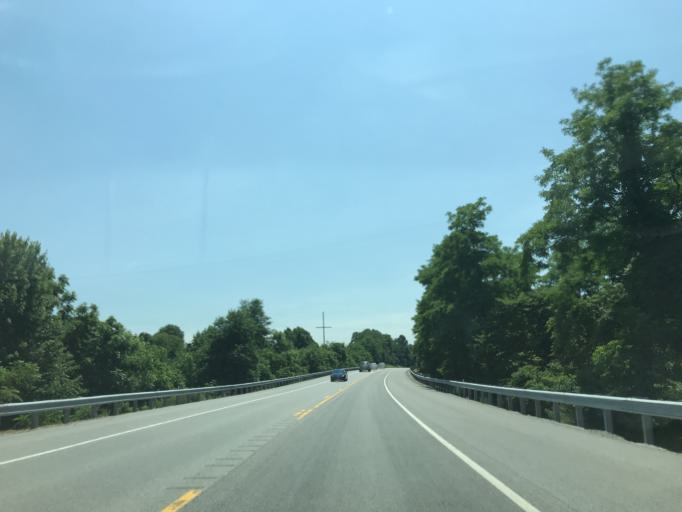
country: US
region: Maryland
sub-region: Carroll County
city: Westminster
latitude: 39.6041
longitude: -76.9440
